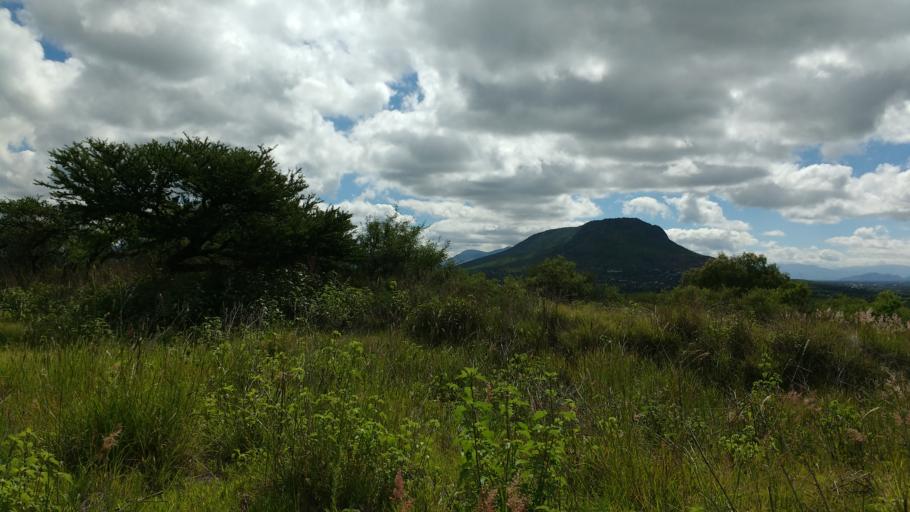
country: MX
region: Hidalgo
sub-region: Tezontepec de Aldama
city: Tenango
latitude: 20.2491
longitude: -99.2761
